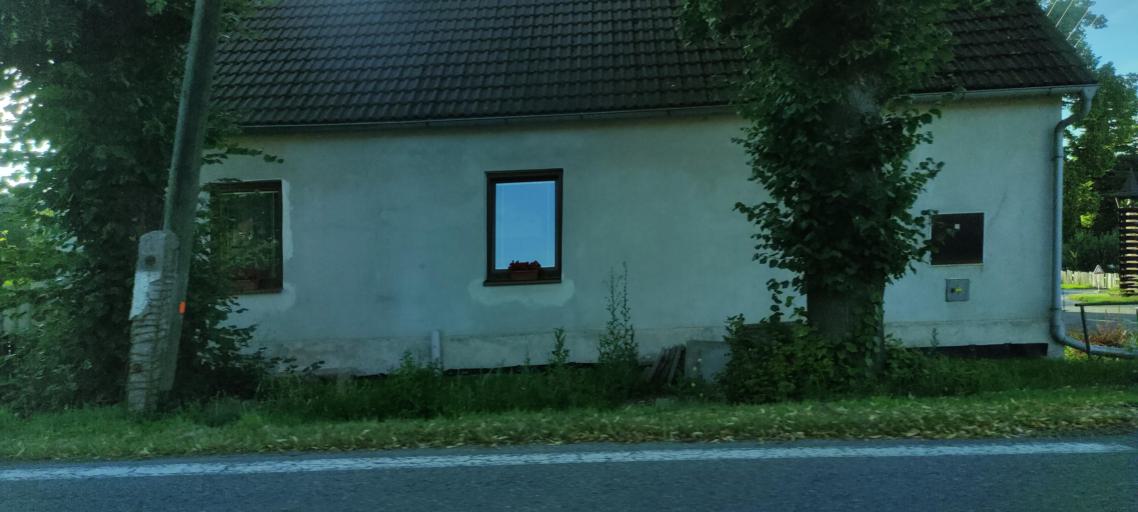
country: CZ
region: Jihocesky
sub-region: Okres Jindrichuv Hradec
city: Jindrichuv Hradec
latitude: 49.1122
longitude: 14.9960
